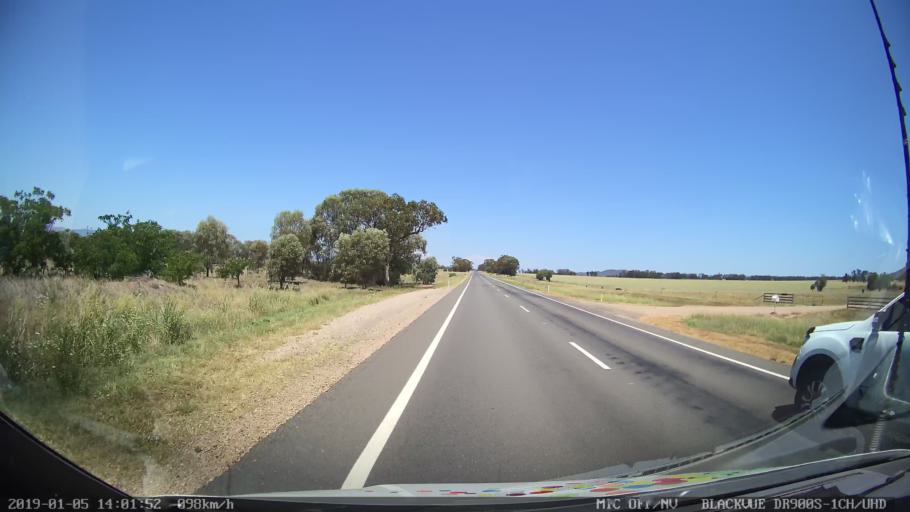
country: AU
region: New South Wales
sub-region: Gunnedah
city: Gunnedah
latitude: -31.1740
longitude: 150.3305
